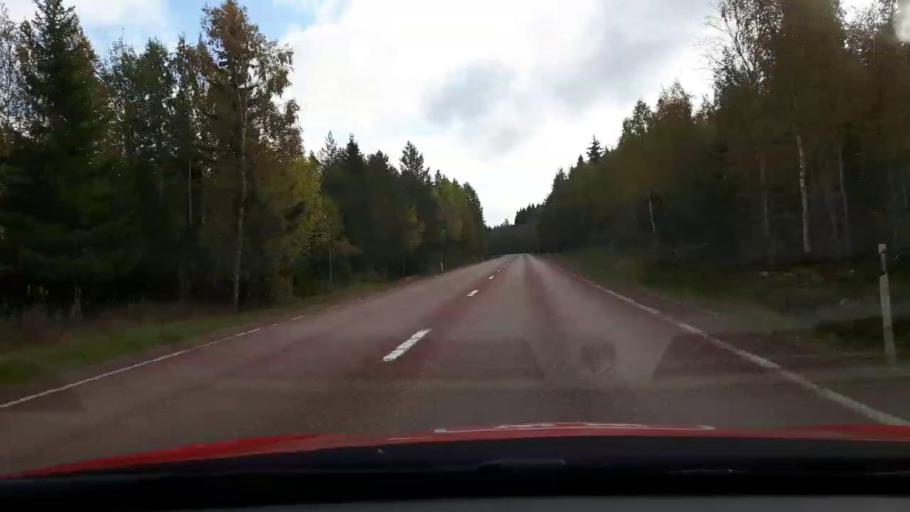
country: SE
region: Gaevleborg
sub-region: Ljusdals Kommun
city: Jaervsoe
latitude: 61.6403
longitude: 16.2342
